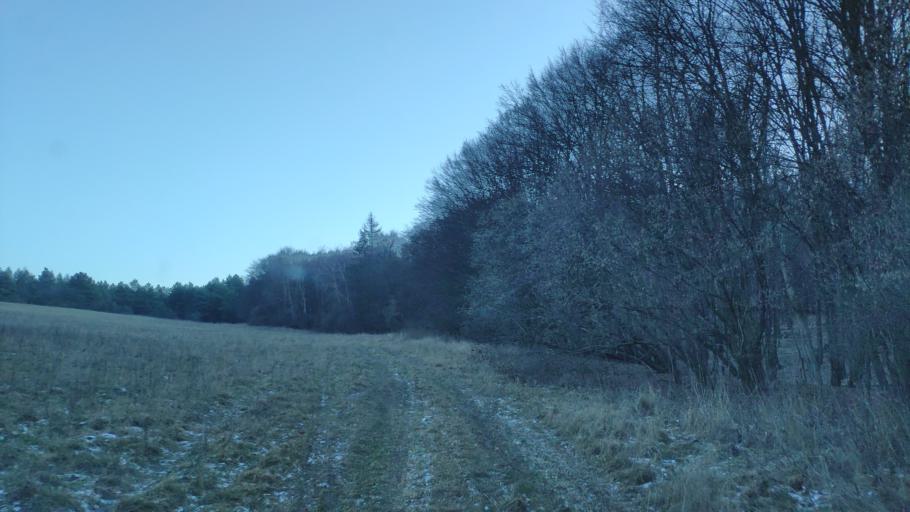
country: SK
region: Kosicky
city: Kosice
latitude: 48.8474
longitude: 21.2427
